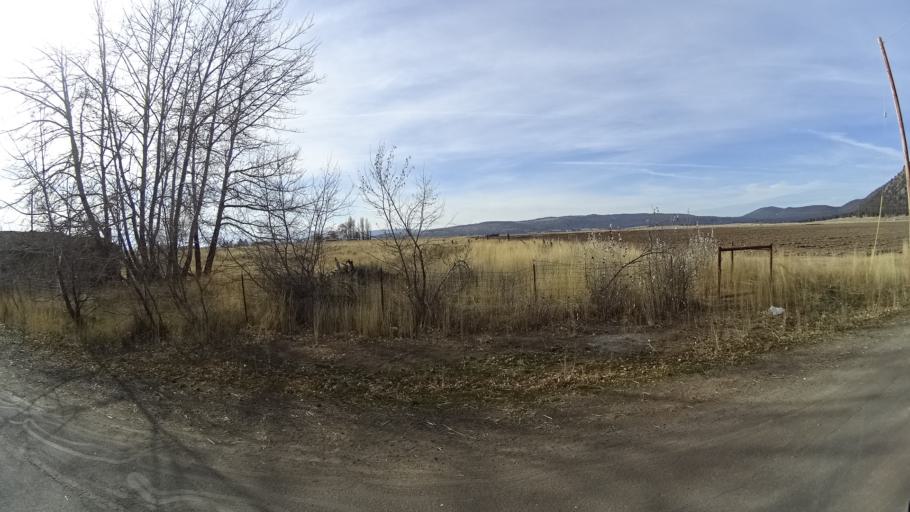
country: US
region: Oregon
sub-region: Klamath County
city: Klamath Falls
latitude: 41.9714
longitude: -121.9214
